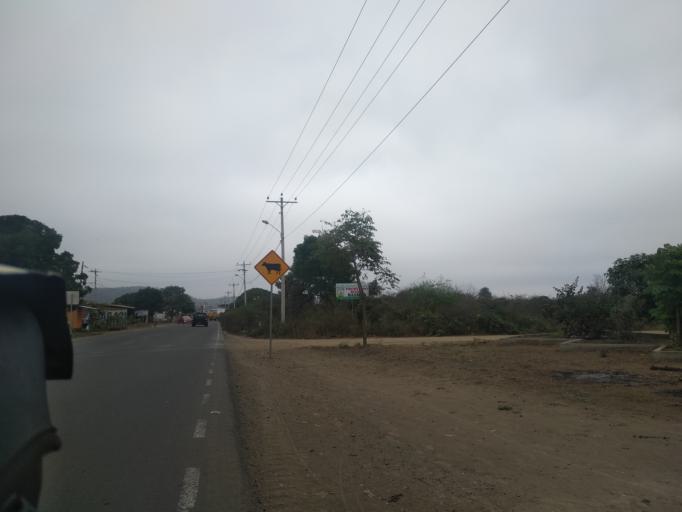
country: EC
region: Manabi
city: Montecristi
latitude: -1.0813
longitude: -80.6764
